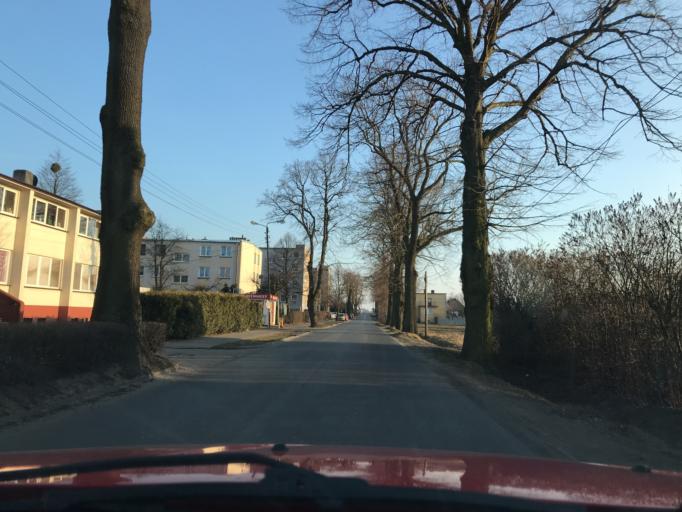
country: PL
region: Greater Poland Voivodeship
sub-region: Powiat jarocinski
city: Kotlin
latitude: 51.9168
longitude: 17.6527
